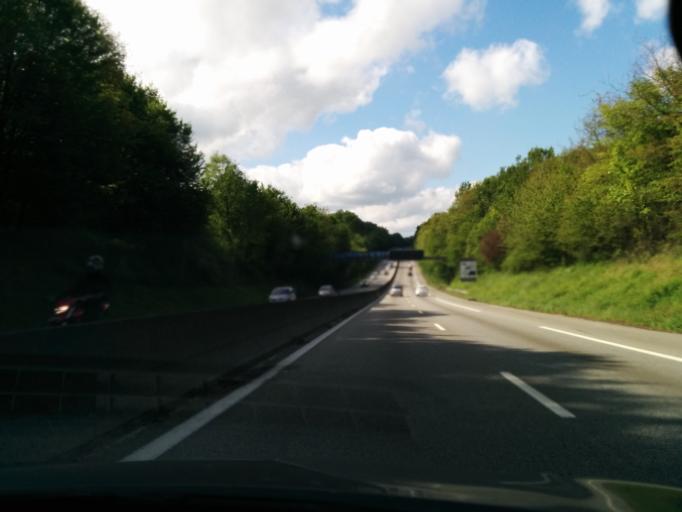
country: FR
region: Ile-de-France
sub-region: Departement des Yvelines
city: Chambourcy
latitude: 48.8924
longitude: 2.0087
